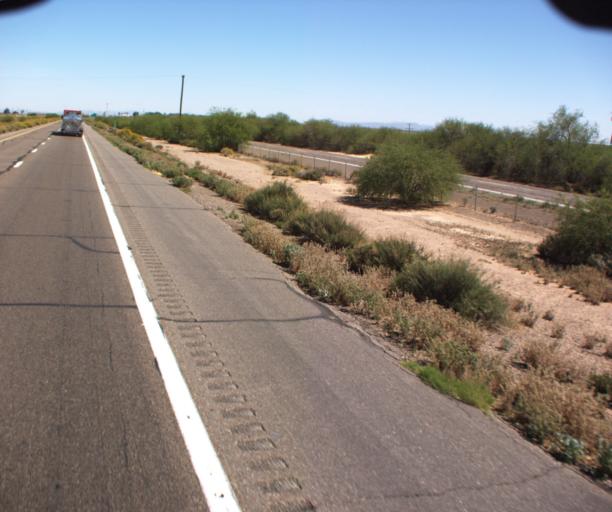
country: US
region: Arizona
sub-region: Maricopa County
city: Gila Bend
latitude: 32.9172
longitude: -112.9147
